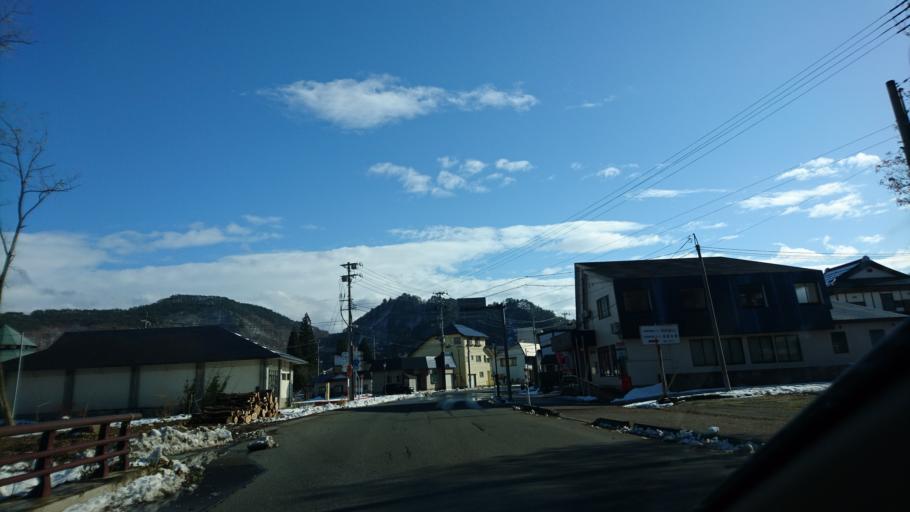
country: JP
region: Akita
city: Yokotemachi
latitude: 39.3138
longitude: 140.7774
